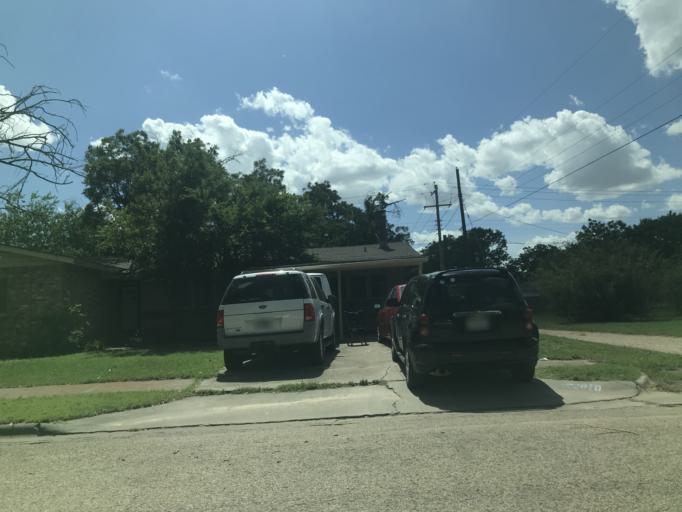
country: US
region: Texas
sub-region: Taylor County
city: Abilene
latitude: 32.4247
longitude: -99.7624
